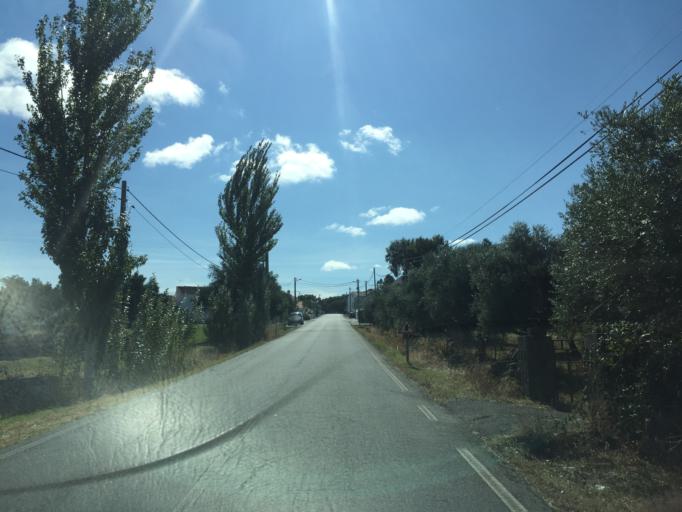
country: PT
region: Portalegre
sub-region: Marvao
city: Marvao
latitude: 39.4357
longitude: -7.3644
